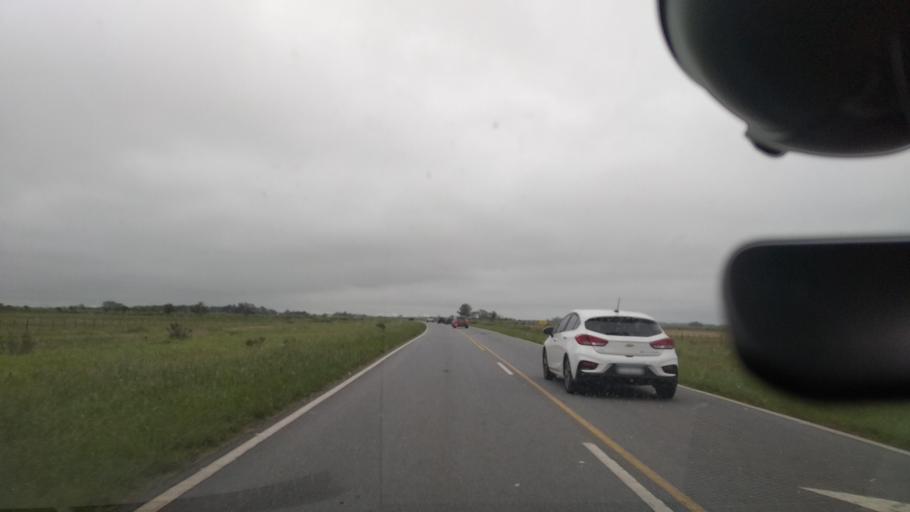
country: AR
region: Buenos Aires
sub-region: Partido de Magdalena
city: Magdalena
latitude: -35.2483
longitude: -57.6707
